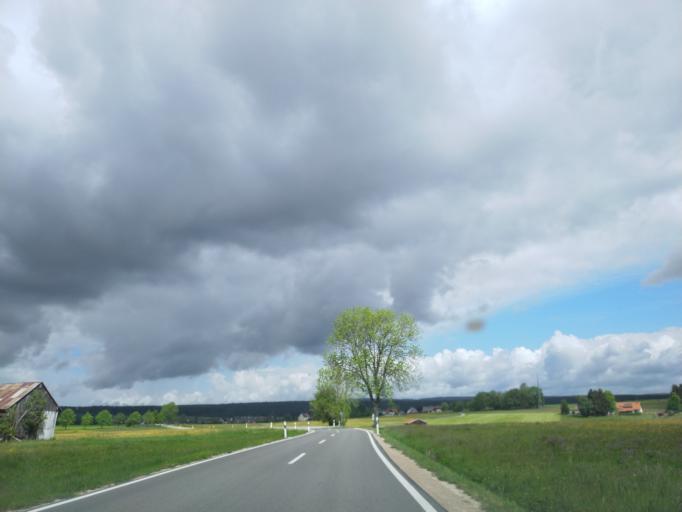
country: DE
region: Baden-Wuerttemberg
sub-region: Freiburg Region
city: Loffingen
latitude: 47.8837
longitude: 8.3051
